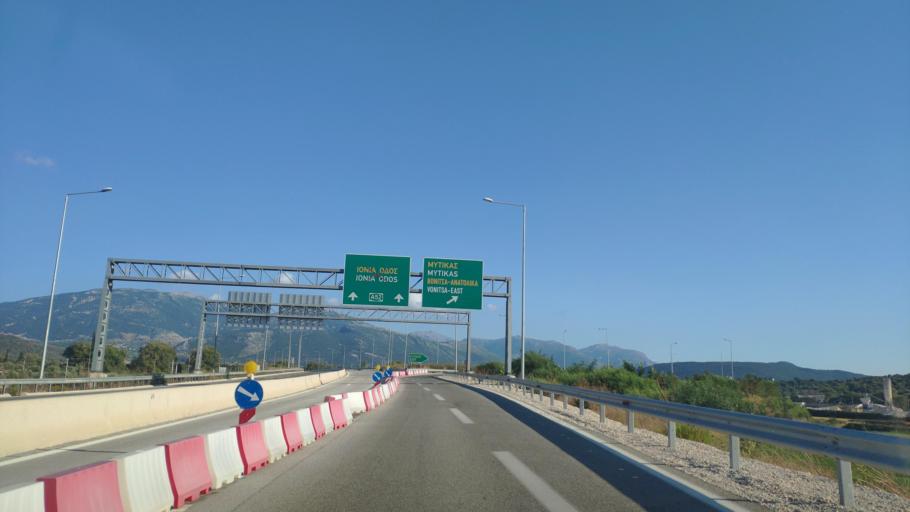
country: GR
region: West Greece
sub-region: Nomos Aitolias kai Akarnanias
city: Vonitsa
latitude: 38.8924
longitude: 20.8981
